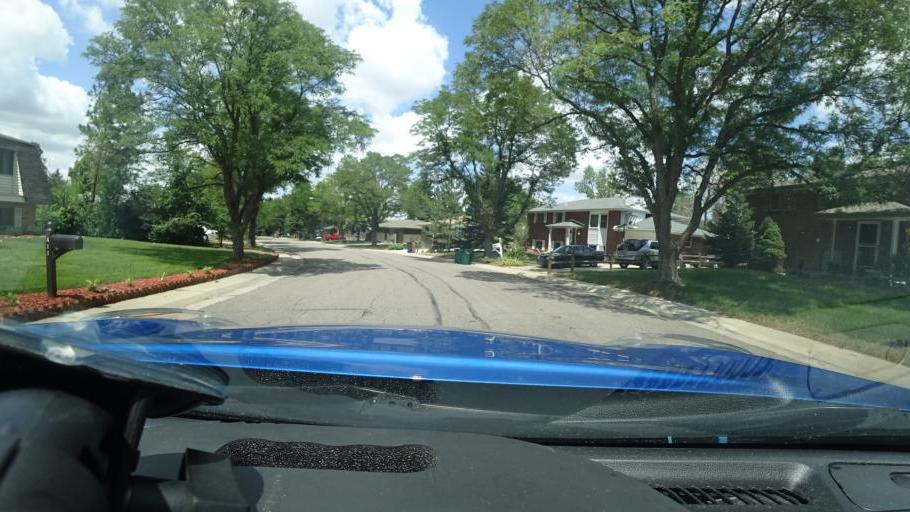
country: US
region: Colorado
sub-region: Adams County
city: Aurora
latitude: 39.7069
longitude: -104.8370
